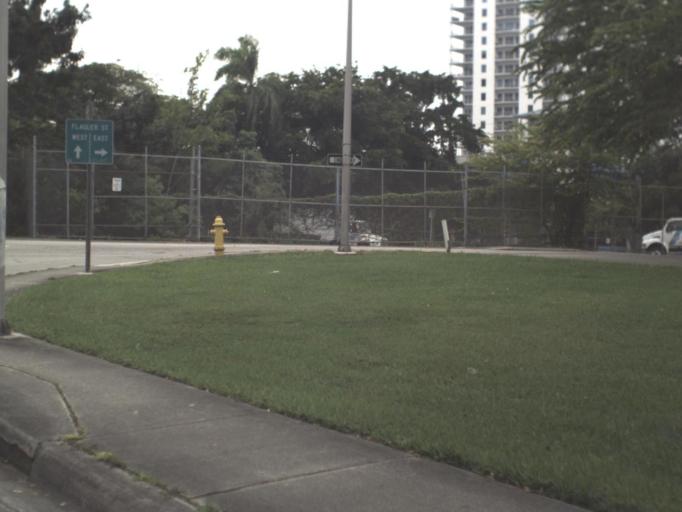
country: US
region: Florida
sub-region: Miami-Dade County
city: Miami
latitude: 25.7751
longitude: -80.2002
